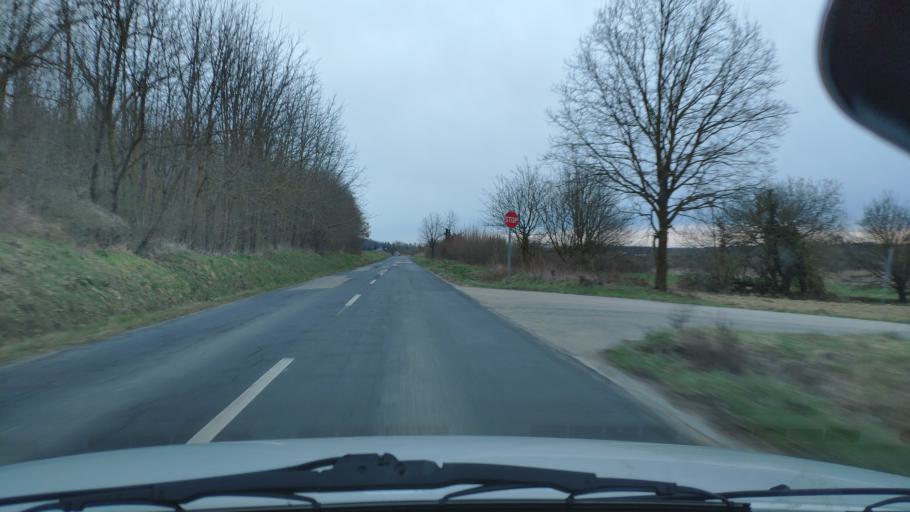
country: HU
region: Zala
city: Nagykanizsa
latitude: 46.5283
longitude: 16.9824
